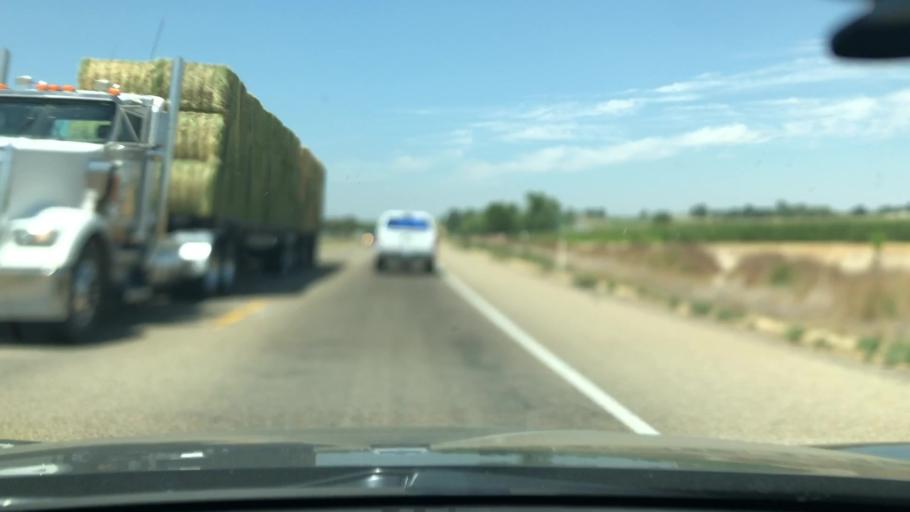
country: US
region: Idaho
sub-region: Canyon County
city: Parma
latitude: 43.8101
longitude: -116.9543
